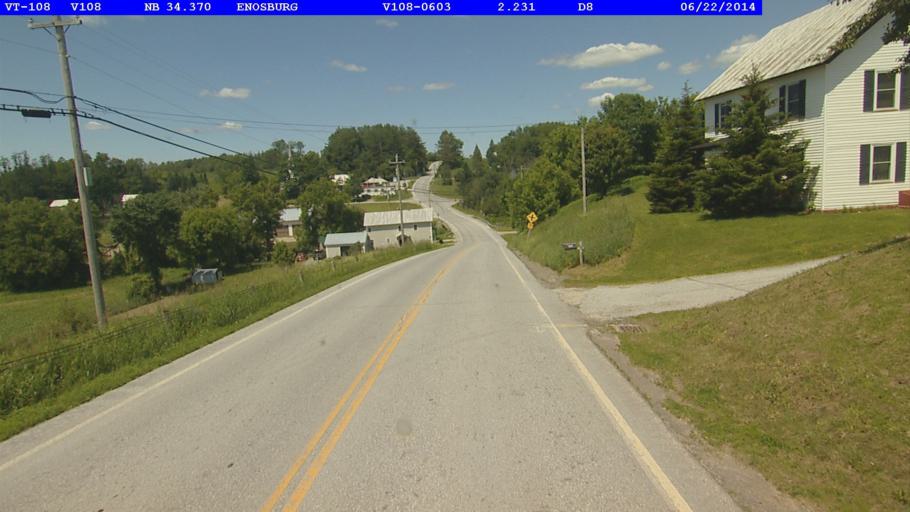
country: US
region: Vermont
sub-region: Franklin County
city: Enosburg Falls
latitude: 44.8695
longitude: -72.7976
